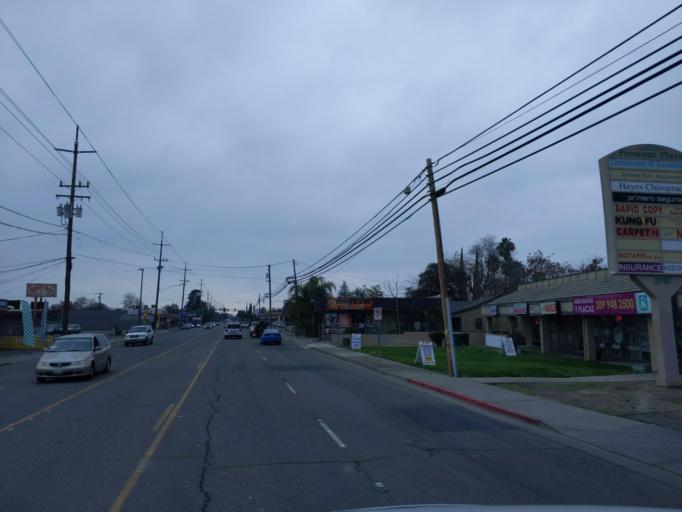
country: US
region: California
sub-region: San Joaquin County
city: August
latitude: 37.9665
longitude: -121.2540
